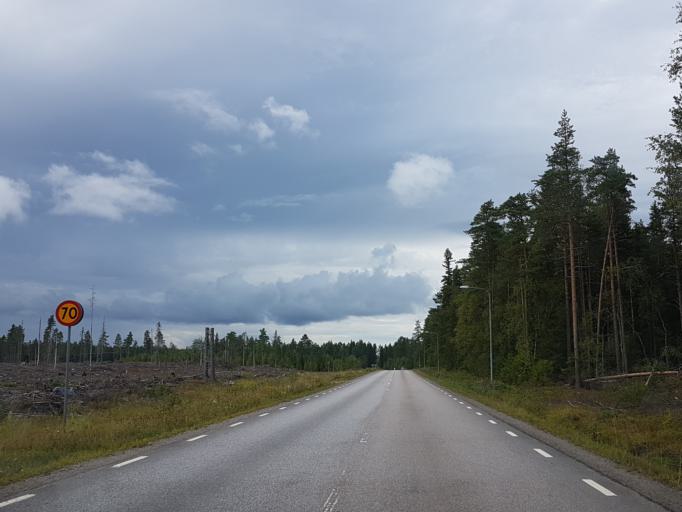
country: SE
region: Vaesterbotten
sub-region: Umea Kommun
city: Holmsund
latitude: 63.7851
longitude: 20.3852
